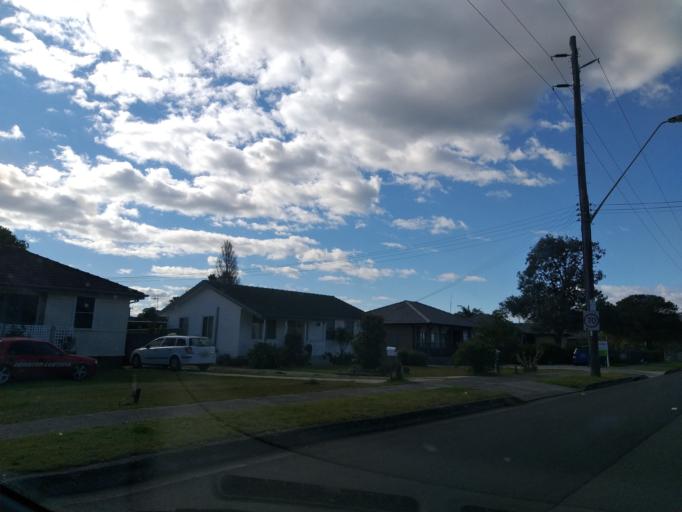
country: AU
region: New South Wales
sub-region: Shellharbour
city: Lake Illawarra
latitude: -34.5534
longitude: 150.8563
